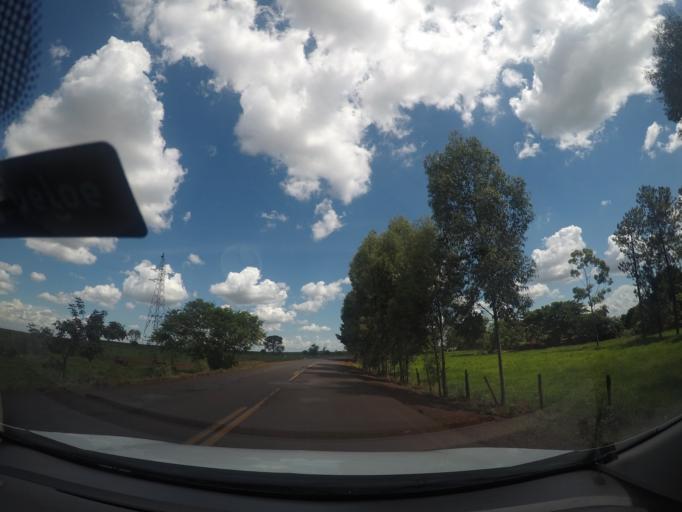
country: BR
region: Minas Gerais
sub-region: Frutal
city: Frutal
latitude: -19.8404
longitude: -48.7361
